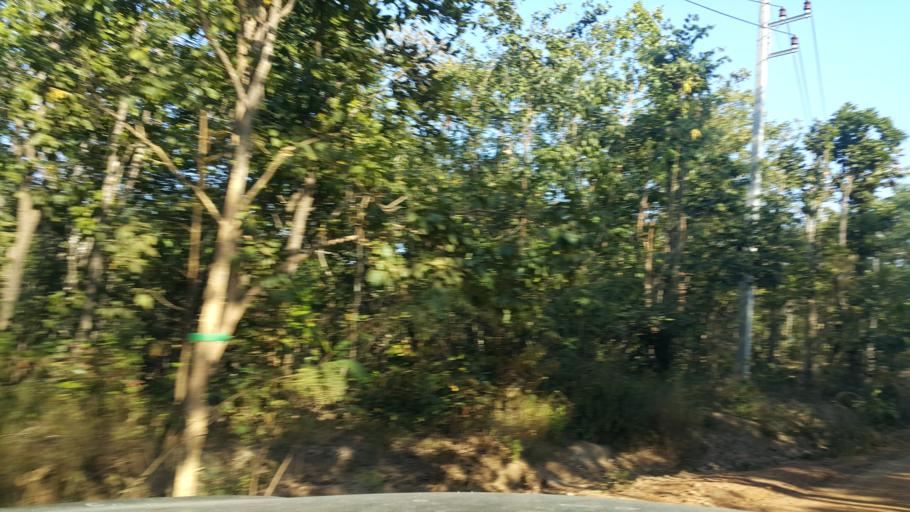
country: TH
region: Lamphun
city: Mae Tha
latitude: 18.5237
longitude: 99.1167
